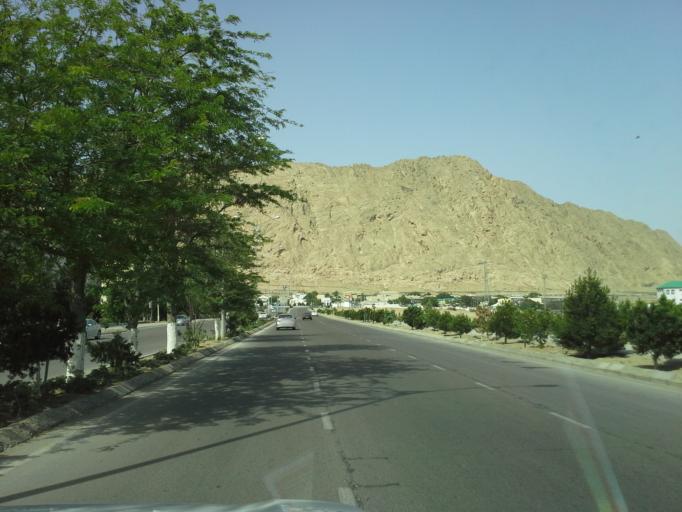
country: TM
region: Balkan
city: Turkmenbasy
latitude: 40.0061
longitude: 52.9973
